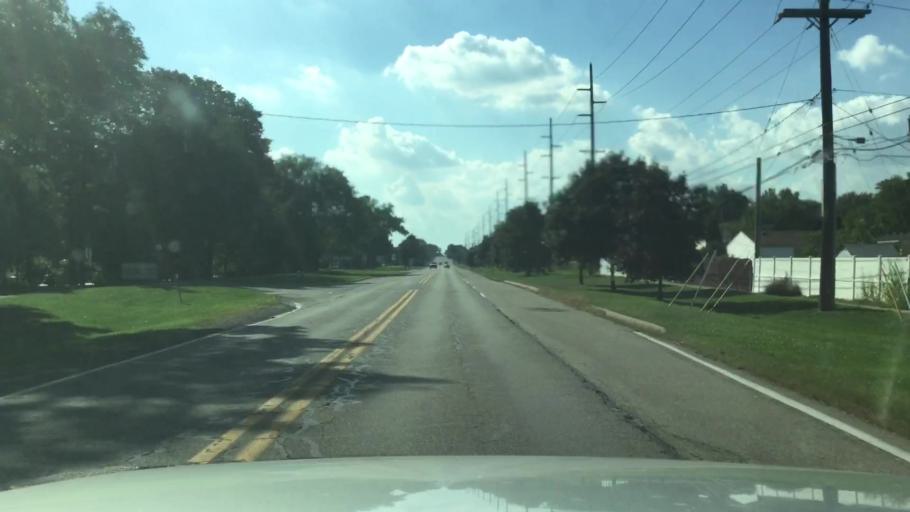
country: US
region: Michigan
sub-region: Wayne County
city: Westland
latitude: 42.3526
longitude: -83.4261
